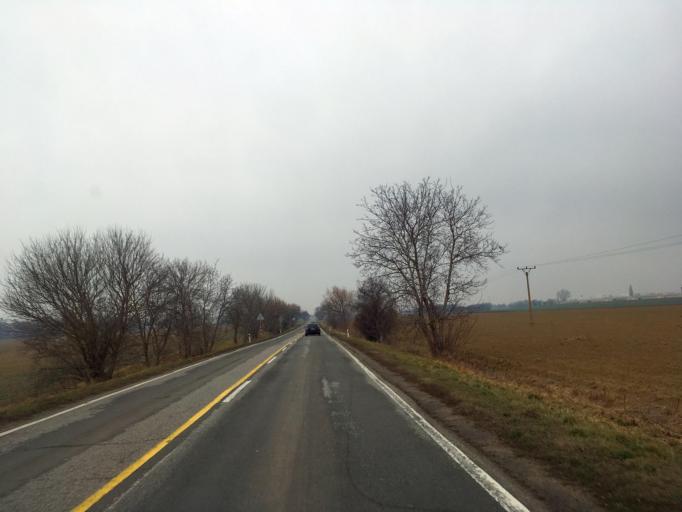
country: SK
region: Nitriansky
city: Sellye
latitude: 48.2331
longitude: 17.8347
